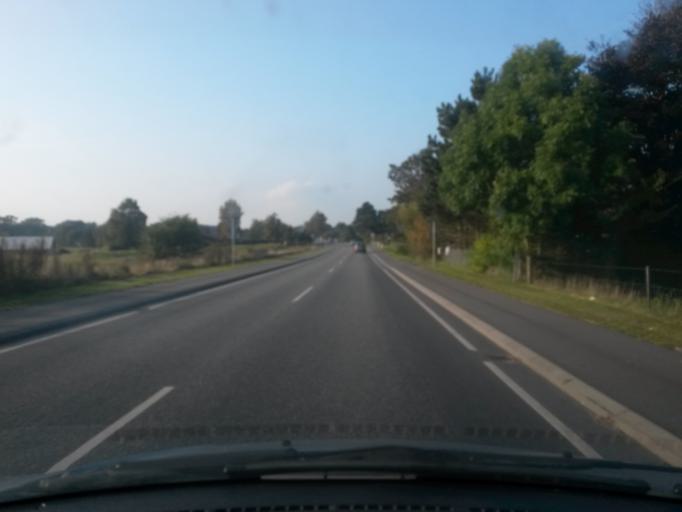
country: DK
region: Central Jutland
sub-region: Syddjurs Kommune
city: Hornslet
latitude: 56.3552
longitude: 10.3439
